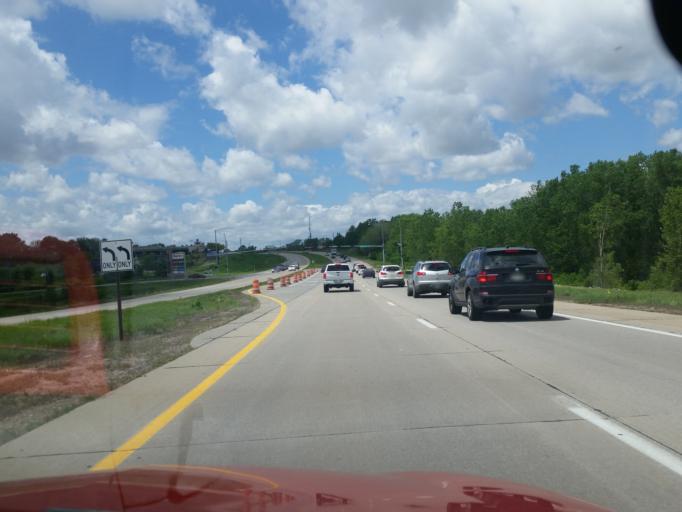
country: US
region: Nebraska
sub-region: Sarpy County
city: Papillion
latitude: 41.1385
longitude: -96.0278
